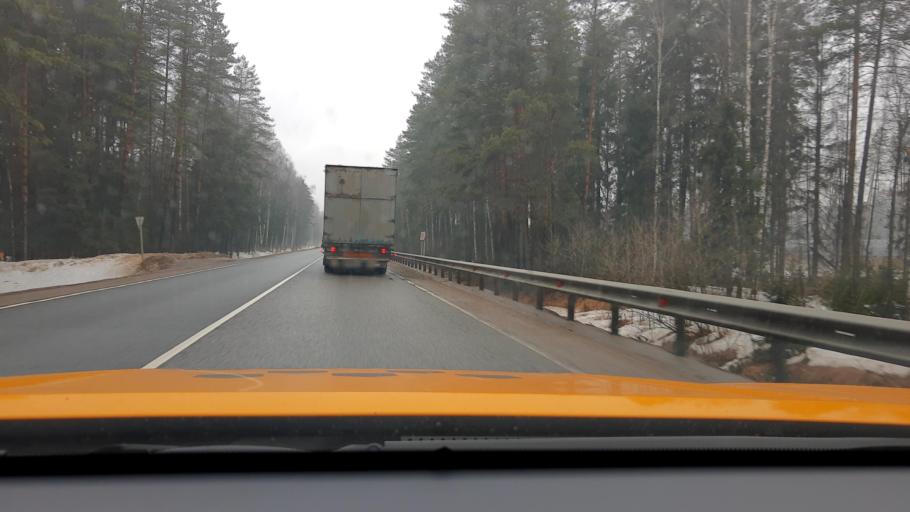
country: RU
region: Moskovskaya
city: Chernogolovka
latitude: 56.0150
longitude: 38.2573
